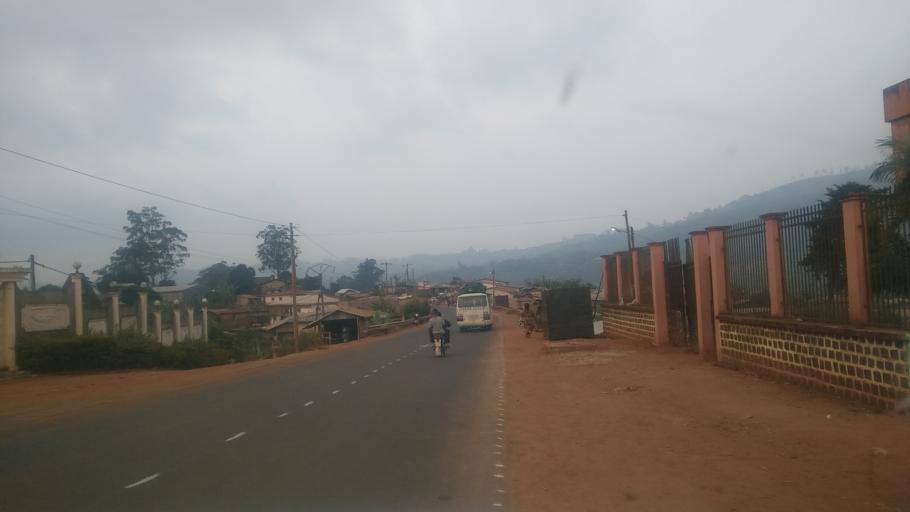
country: CM
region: West
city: Bana
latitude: 5.1460
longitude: 10.2754
